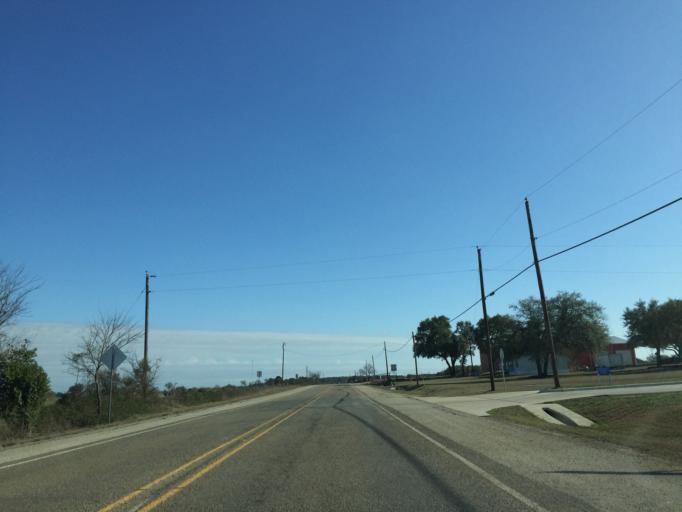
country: US
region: Texas
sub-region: Williamson County
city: Florence
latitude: 30.7802
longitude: -97.8516
